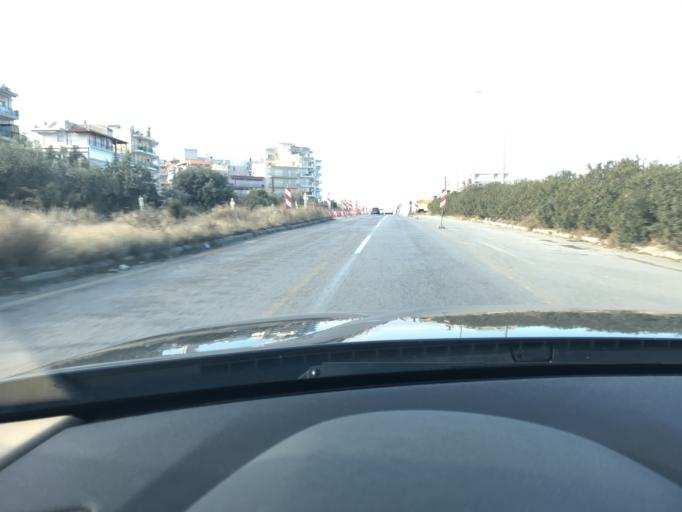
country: GR
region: Central Macedonia
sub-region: Nomos Thessalonikis
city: Stavroupoli
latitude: 40.6773
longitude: 22.9297
